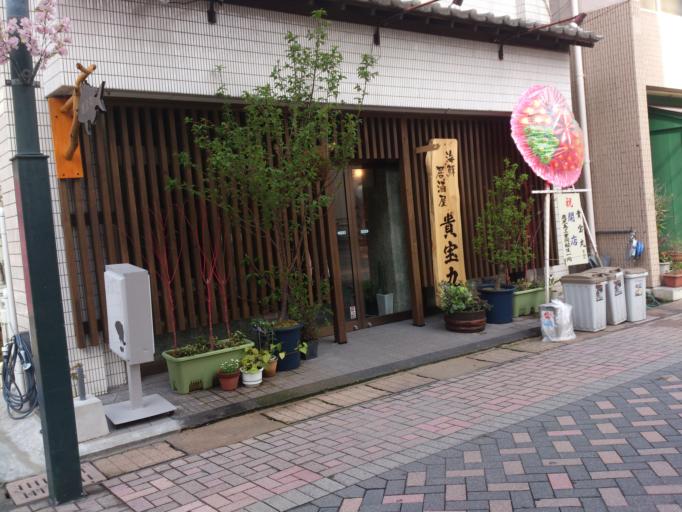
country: JP
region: Kagoshima
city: Kagoshima-shi
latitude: 31.5810
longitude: 130.5422
